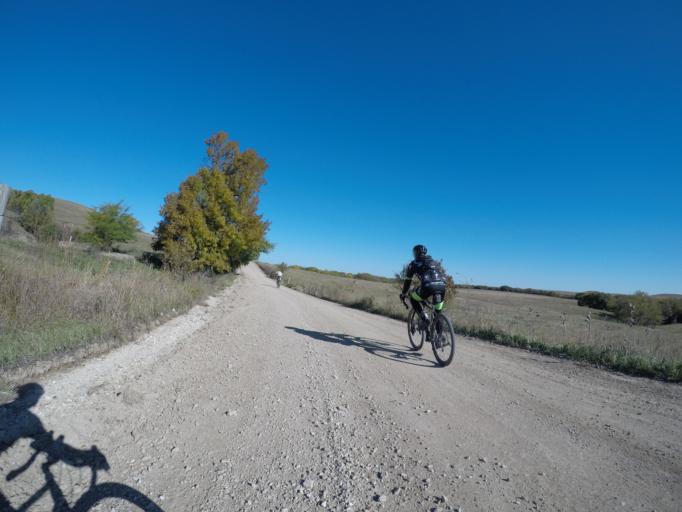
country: US
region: Kansas
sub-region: Wabaunsee County
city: Alma
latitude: 38.8845
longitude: -96.3614
